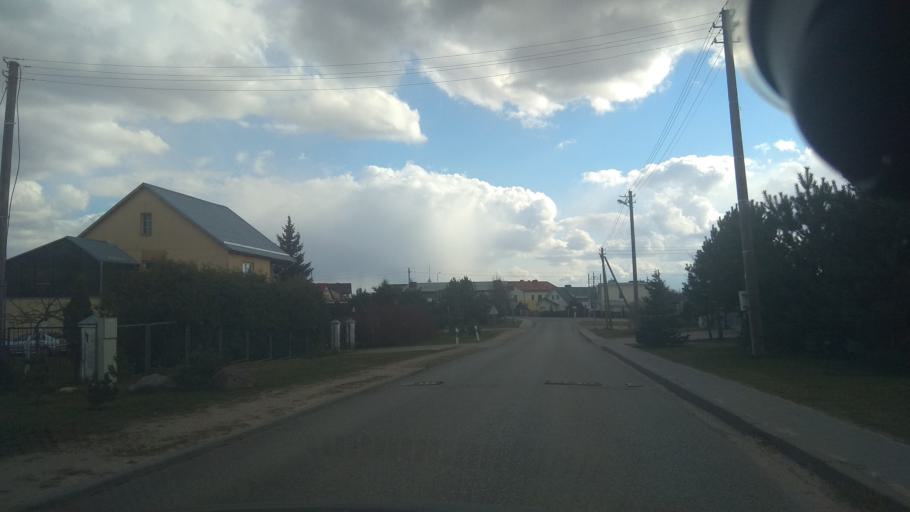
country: LT
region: Vilnius County
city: Pasilaiciai
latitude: 54.7370
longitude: 25.2020
